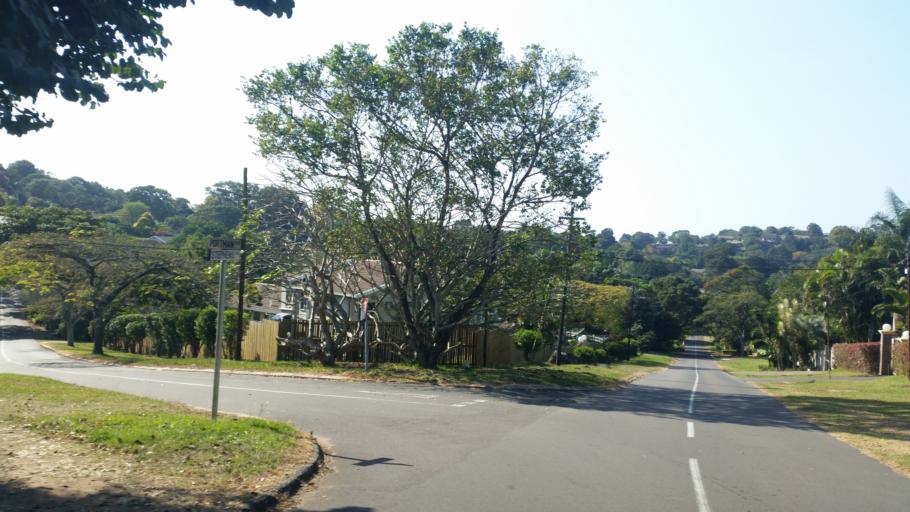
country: ZA
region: KwaZulu-Natal
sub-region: eThekwini Metropolitan Municipality
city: Berea
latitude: -29.8456
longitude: 30.9013
